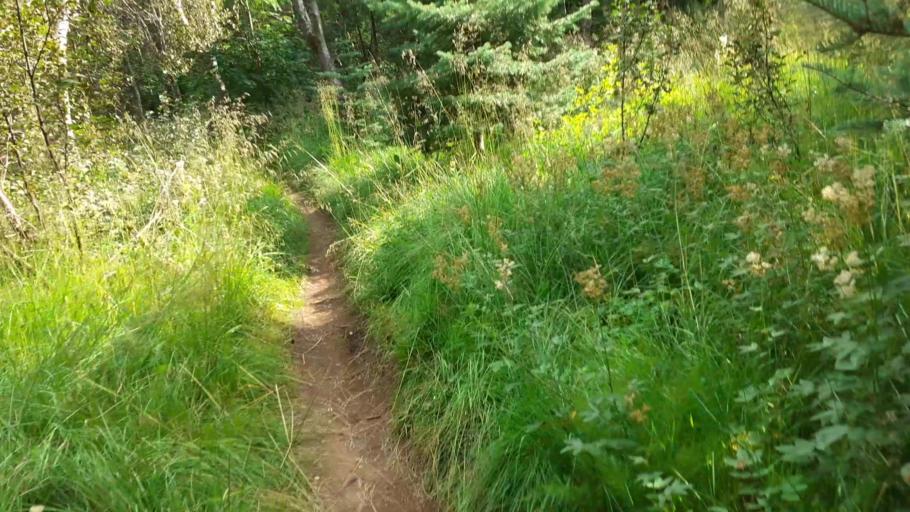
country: IS
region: Northeast
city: Akureyri
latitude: 65.6426
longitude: -18.0859
